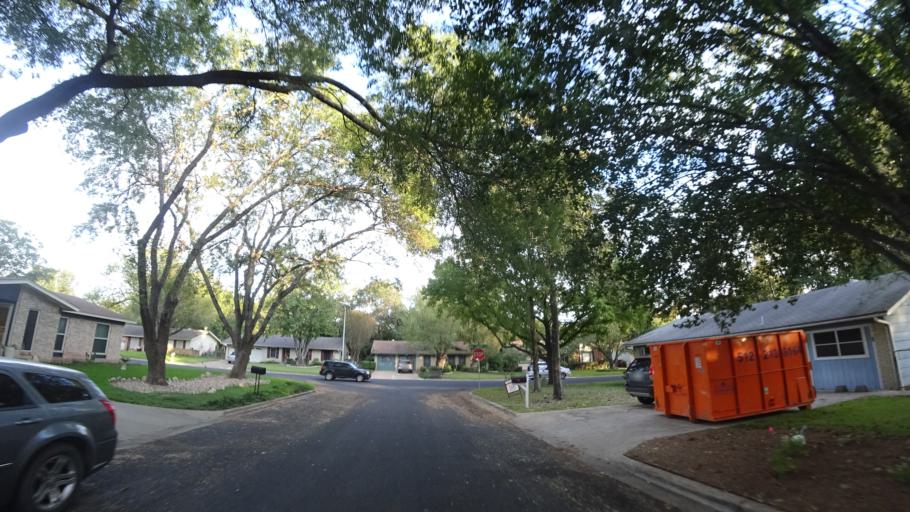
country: US
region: Texas
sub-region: Travis County
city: Austin
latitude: 30.2120
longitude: -97.7632
